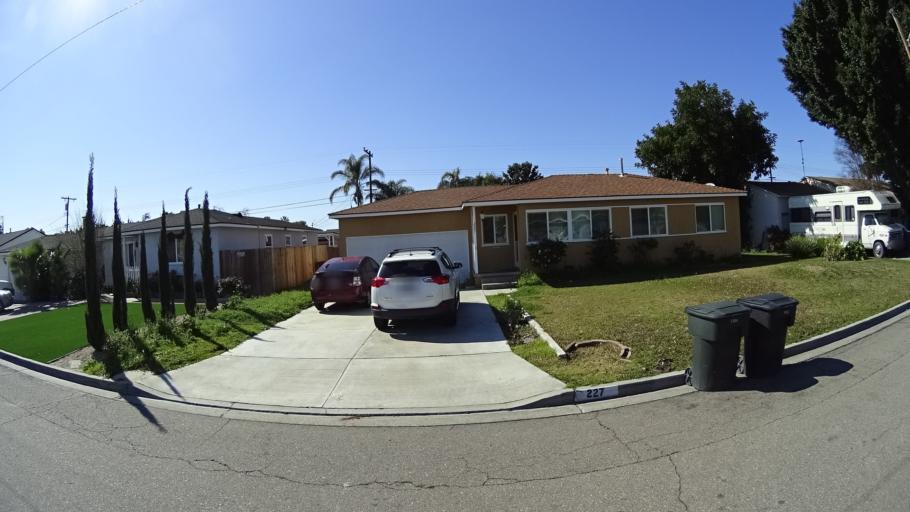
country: US
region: California
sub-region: Orange County
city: Anaheim
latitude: 33.8348
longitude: -117.9517
